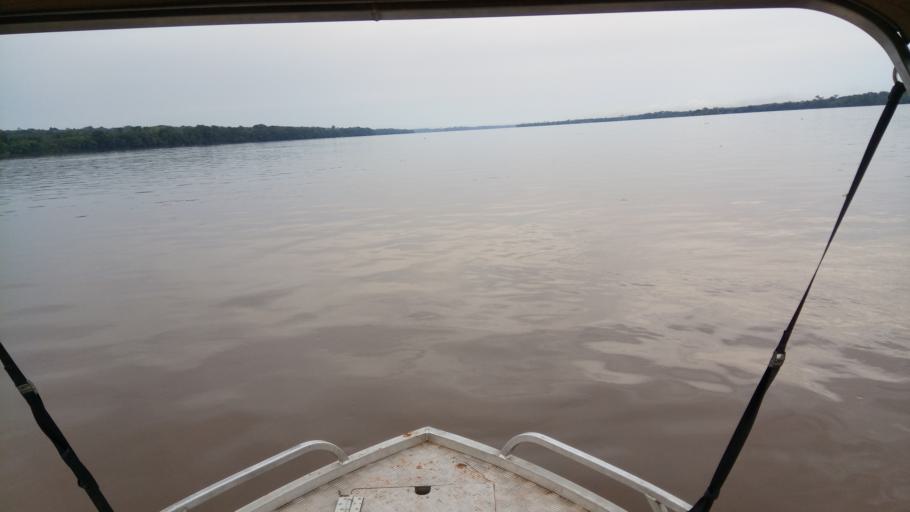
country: CD
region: Eastern Province
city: Kisangani
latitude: 0.5726
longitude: 24.8455
